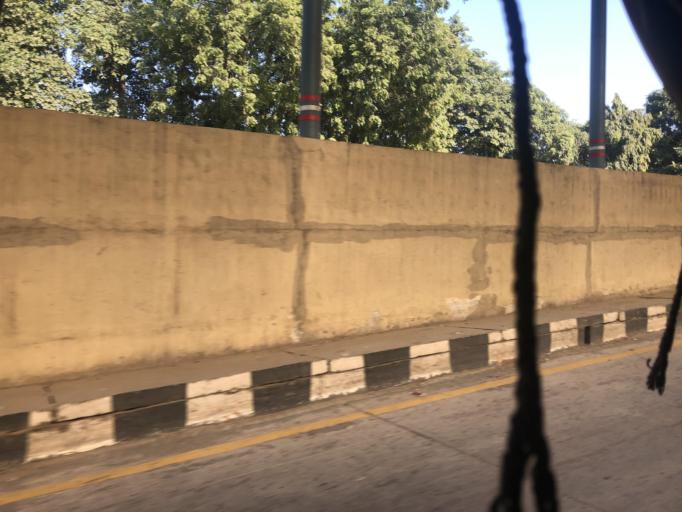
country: IN
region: Haryana
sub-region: Gurgaon
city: Gurgaon
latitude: 28.4666
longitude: 77.0606
